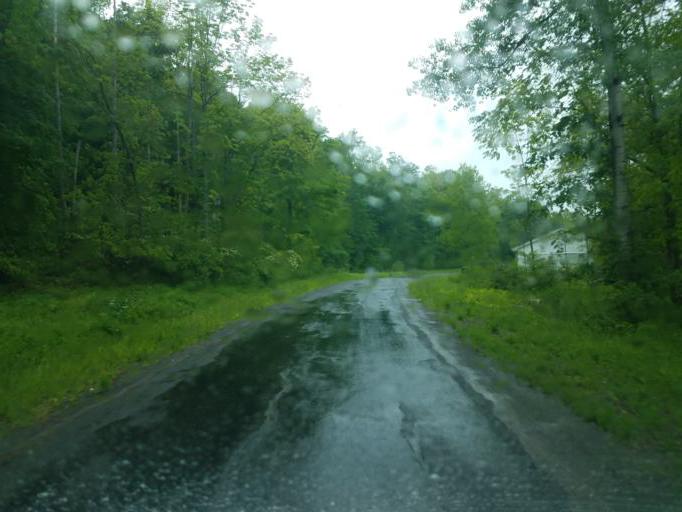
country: US
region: New York
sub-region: Herkimer County
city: Ilion
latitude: 42.9571
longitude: -75.0310
